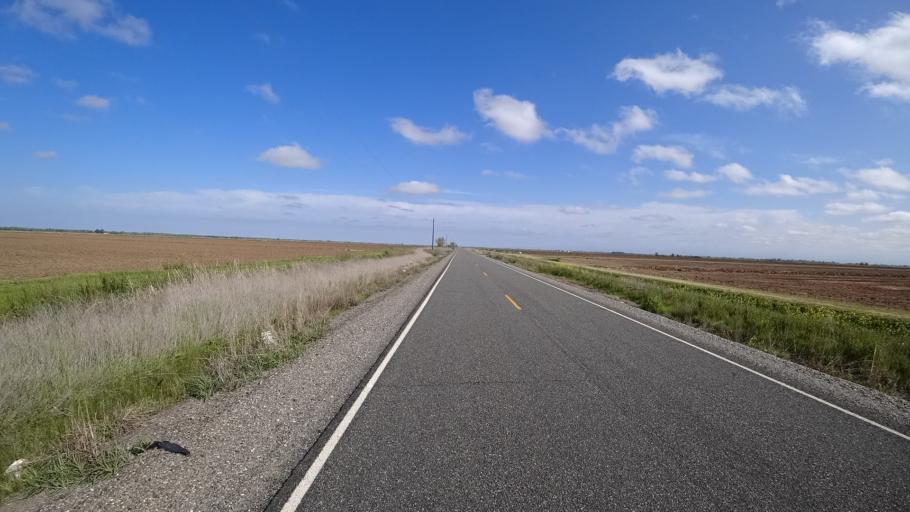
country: US
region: California
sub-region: Butte County
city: Durham
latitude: 39.5068
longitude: -121.9299
